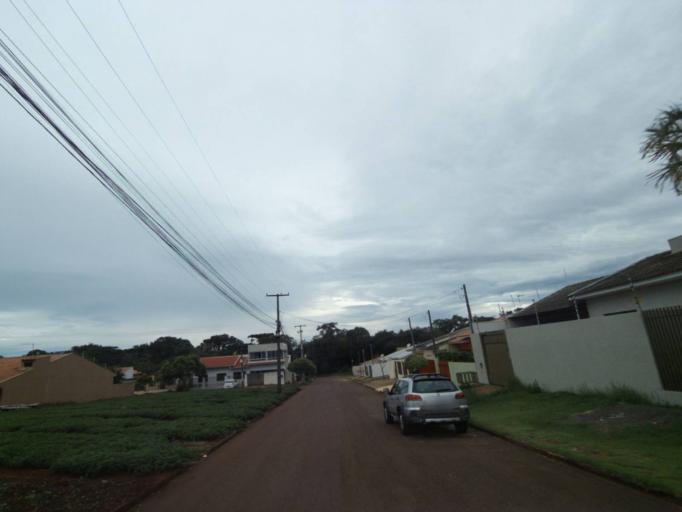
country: BR
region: Parana
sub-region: Campo Mourao
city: Campo Mourao
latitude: -24.0317
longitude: -52.3597
